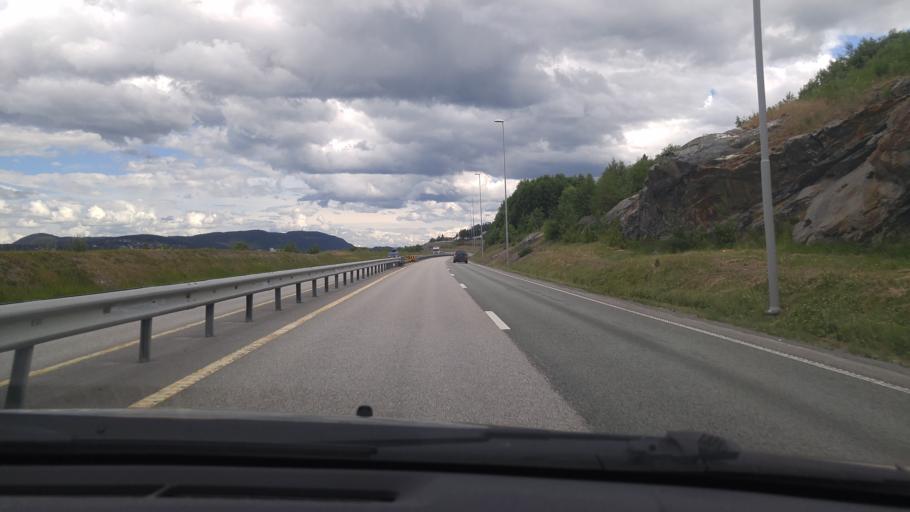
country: NO
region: Nord-Trondelag
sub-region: Steinkjer
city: Steinkjer
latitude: 63.9902
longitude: 11.4501
